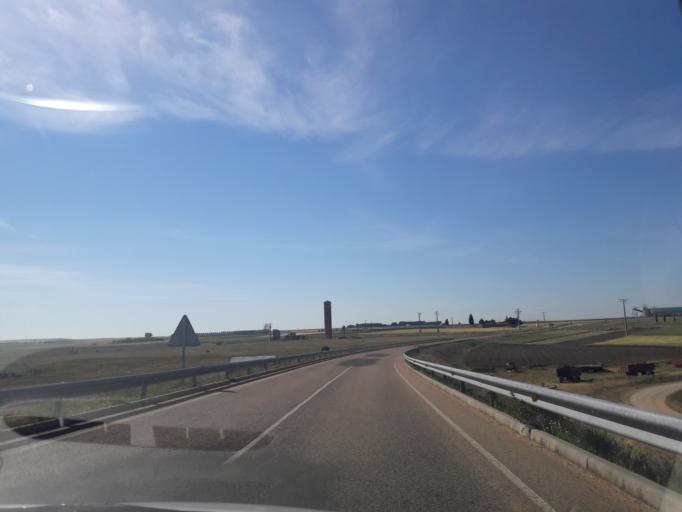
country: ES
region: Castille and Leon
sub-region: Provincia de Salamanca
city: Espino de la Orbada
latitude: 41.0833
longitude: -5.3959
